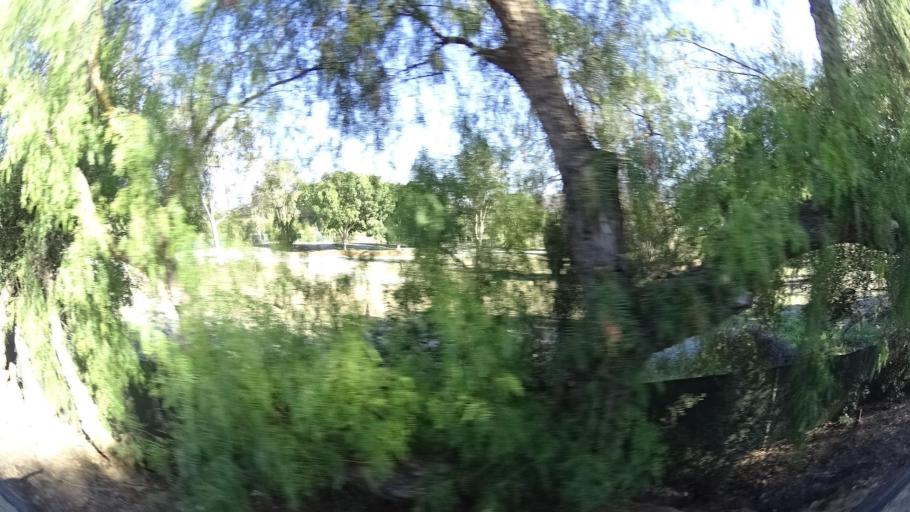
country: US
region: California
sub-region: San Diego County
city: Jamul
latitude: 32.7142
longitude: -116.8756
